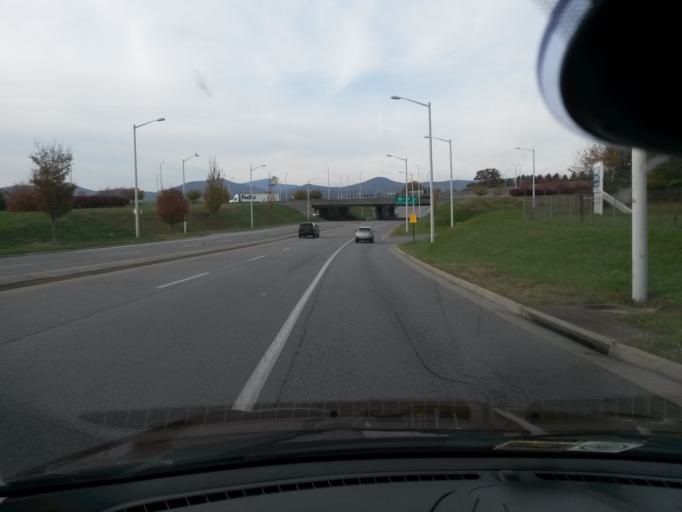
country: US
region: Virginia
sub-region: Roanoke County
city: Hollins
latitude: 37.3116
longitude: -79.9655
